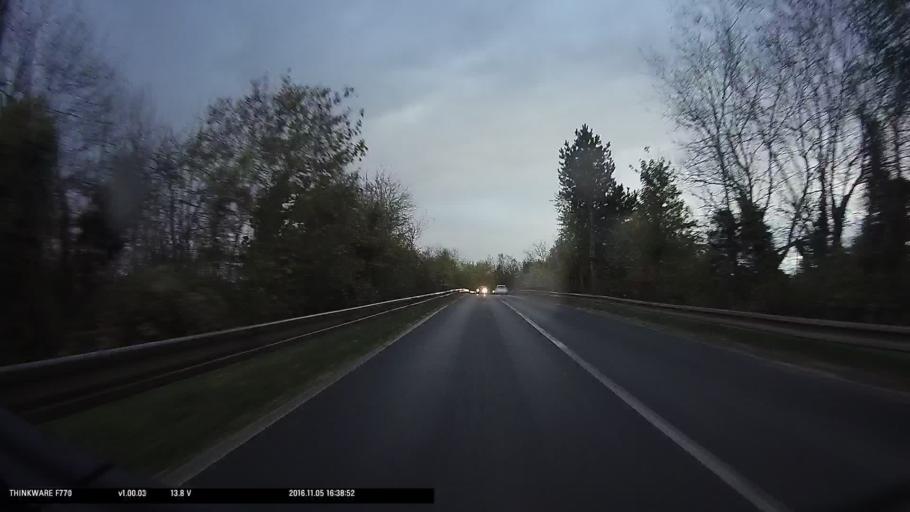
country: FR
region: Ile-de-France
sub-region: Departement du Val-d'Oise
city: Vaureal
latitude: 49.0612
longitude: 2.0200
